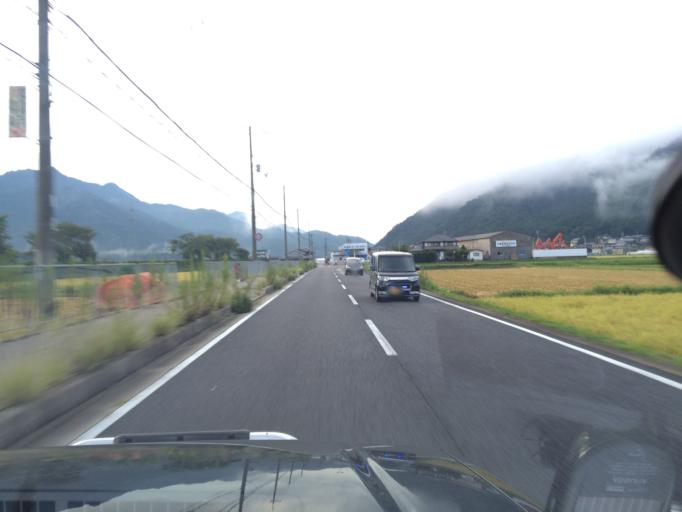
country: JP
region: Hyogo
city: Nishiwaki
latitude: 35.1181
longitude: 135.0032
